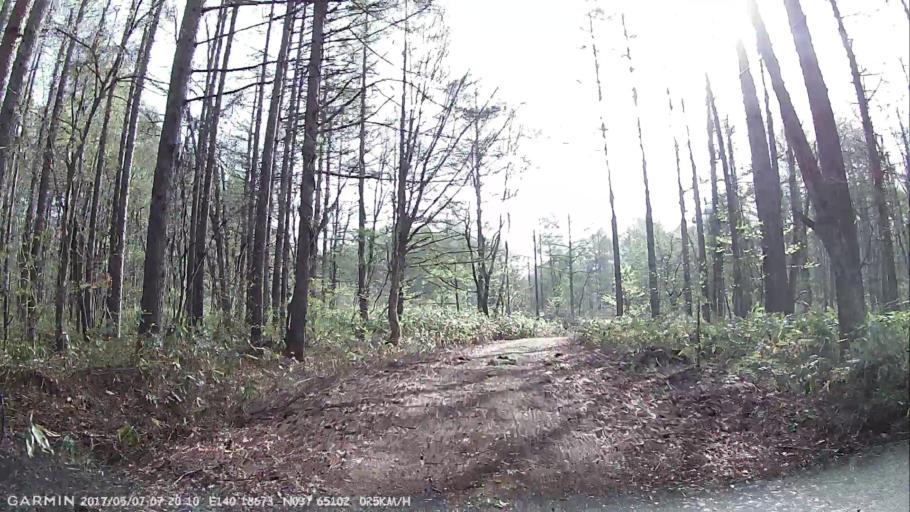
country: JP
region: Fukushima
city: Inawashiro
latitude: 37.6510
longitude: 140.1868
